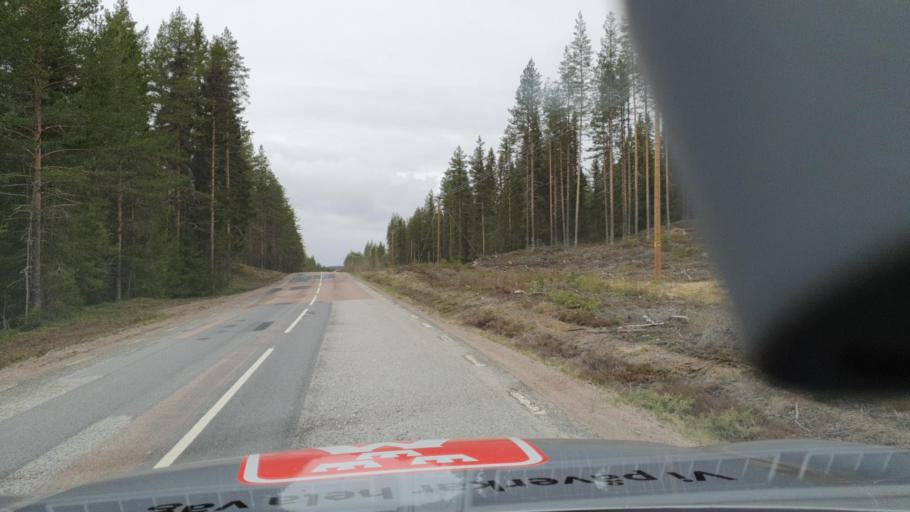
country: SE
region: Vaesternorrland
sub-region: Solleftea Kommun
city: Solleftea
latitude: 63.6307
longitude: 17.4399
